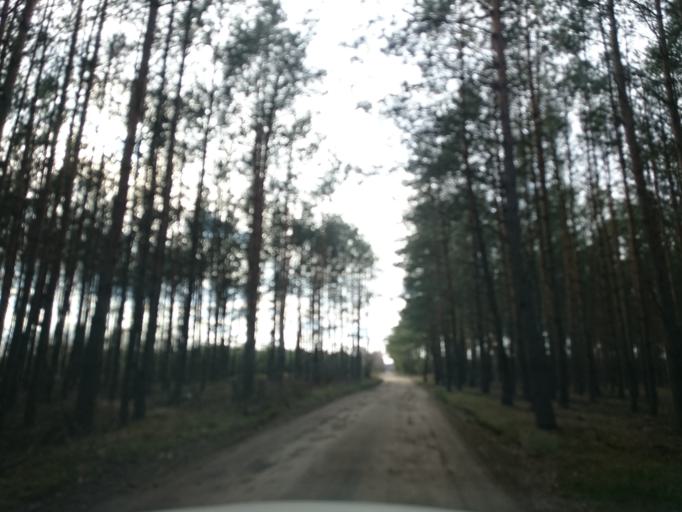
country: PL
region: Kujawsko-Pomorskie
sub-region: Powiat golubsko-dobrzynski
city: Ciechocin
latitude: 53.0503
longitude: 18.8558
